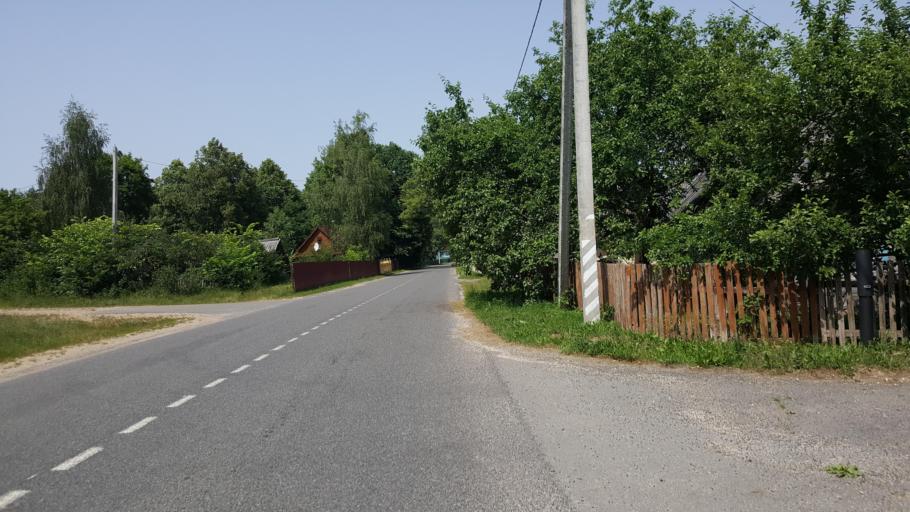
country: BY
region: Brest
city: Kamyanyuki
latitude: 52.5085
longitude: 23.8528
